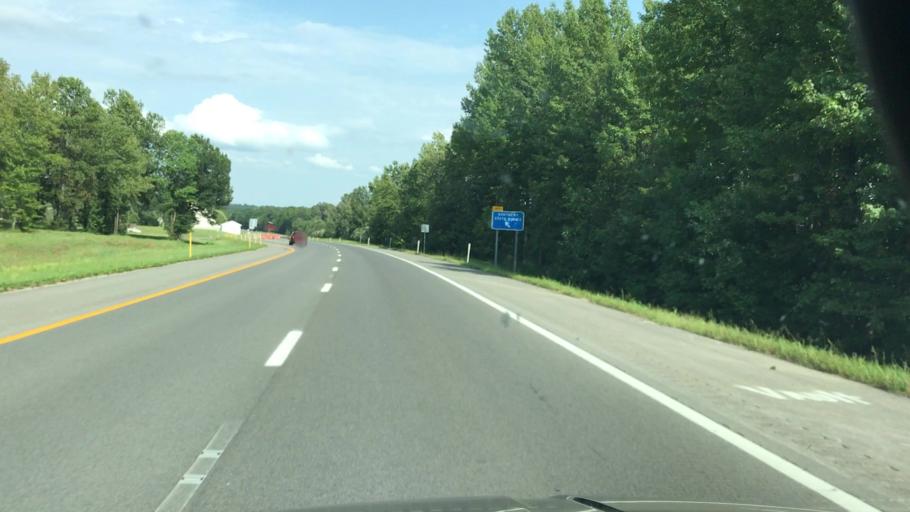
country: US
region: Kentucky
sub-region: Hopkins County
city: Nortonville
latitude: 37.2107
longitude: -87.4203
